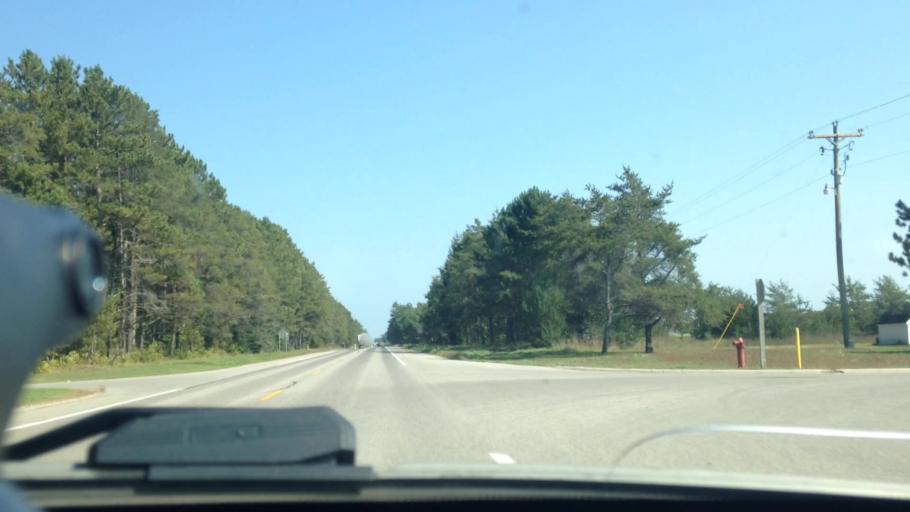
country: US
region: Michigan
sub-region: Luce County
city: Newberry
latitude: 46.3034
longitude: -85.4845
